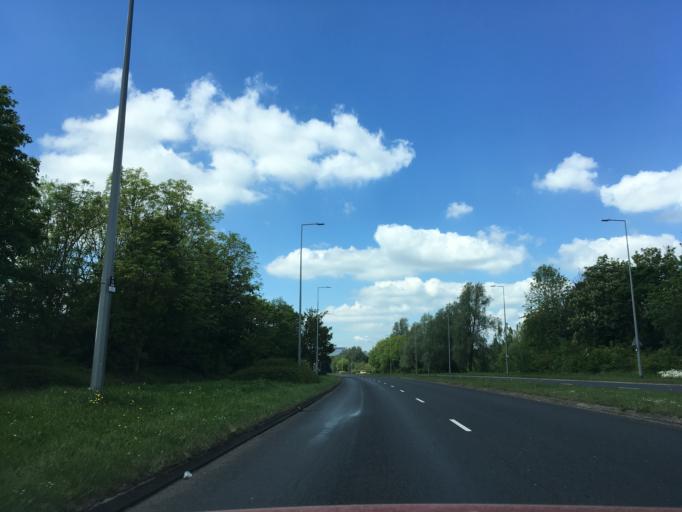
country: GB
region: England
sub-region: Milton Keynes
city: Milton Keynes
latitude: 52.0328
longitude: -0.7476
